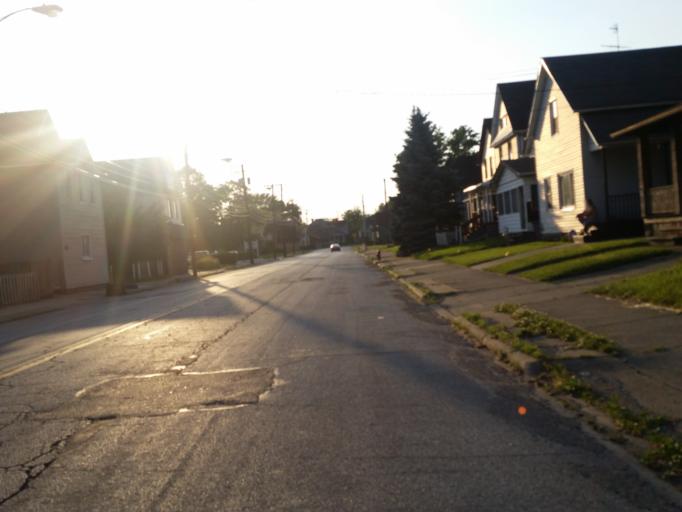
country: US
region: Ohio
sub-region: Cuyahoga County
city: Newburgh Heights
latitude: 41.4591
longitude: -81.6609
